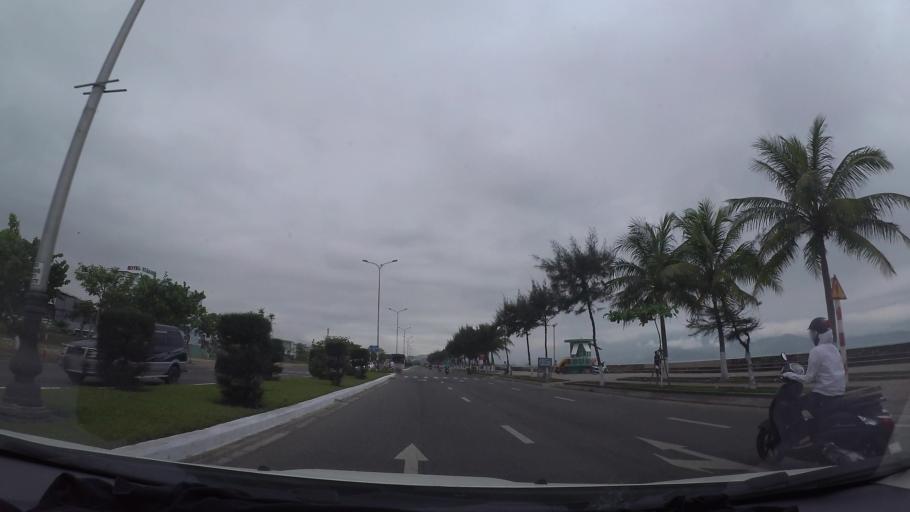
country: VN
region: Da Nang
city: Lien Chieu
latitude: 16.0826
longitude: 108.1642
